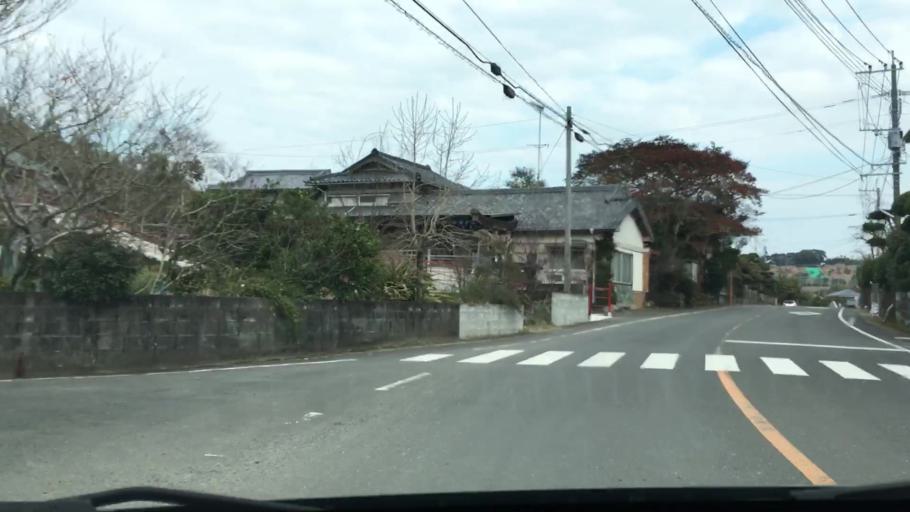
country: JP
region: Miyazaki
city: Kushima
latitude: 31.4678
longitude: 131.2098
